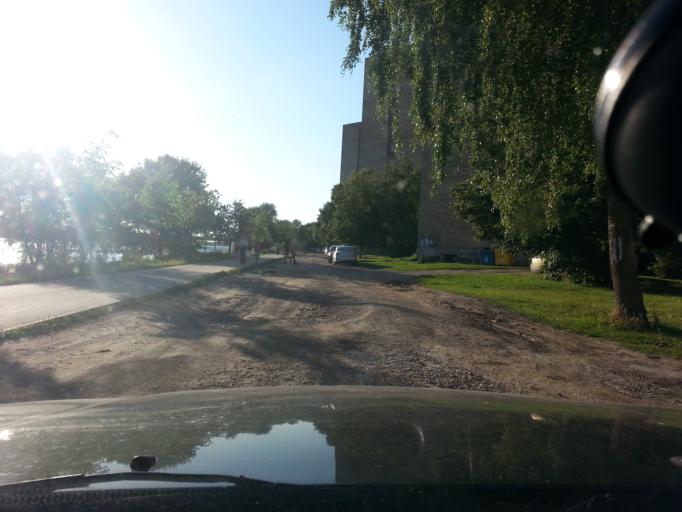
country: LV
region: Kekava
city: Balozi
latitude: 56.9138
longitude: 24.1689
